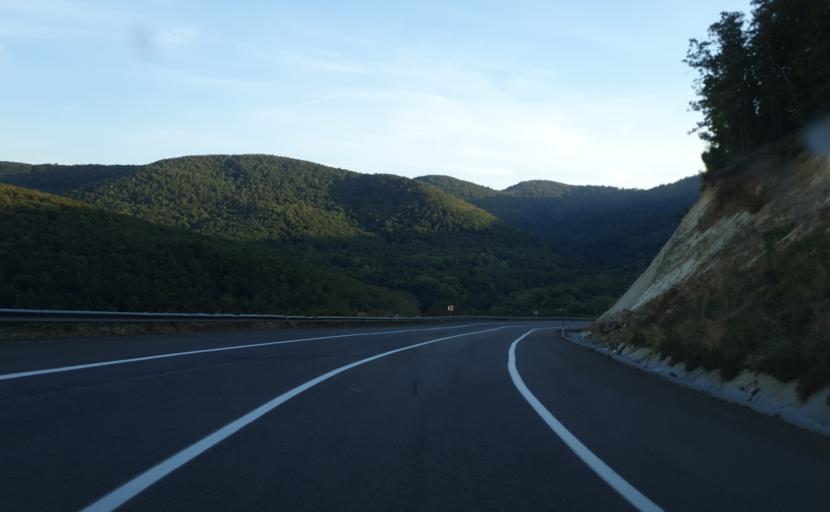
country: TR
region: Kirklareli
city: Sergen
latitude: 41.8126
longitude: 27.7476
